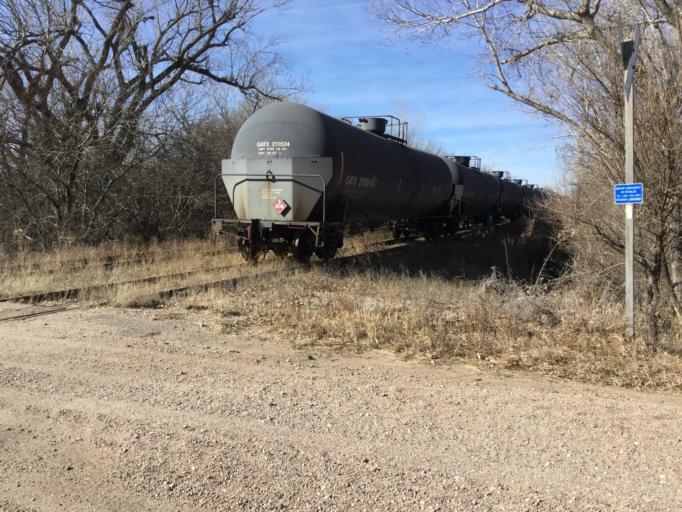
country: US
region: Kansas
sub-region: Rice County
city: Lyons
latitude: 38.5149
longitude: -98.1643
